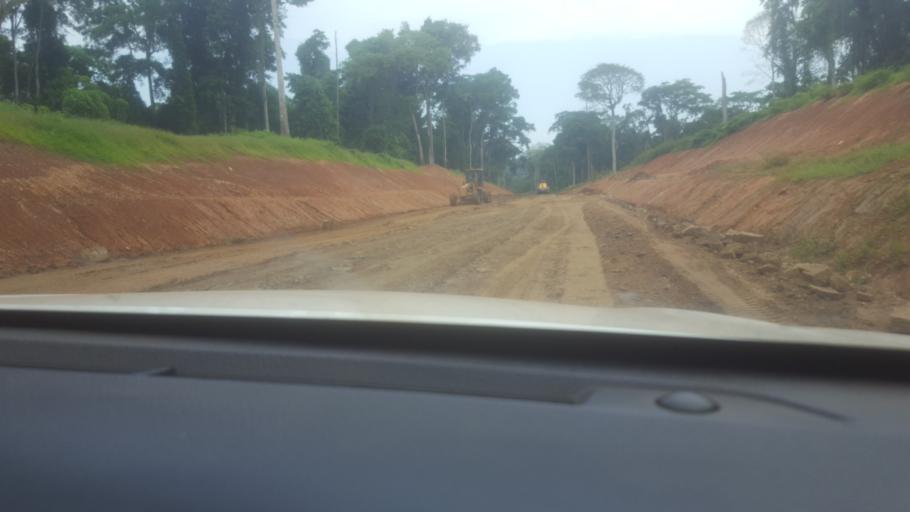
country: ET
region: Southern Nations, Nationalities, and People's Region
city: Tippi
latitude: 7.5188
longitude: 34.9969
